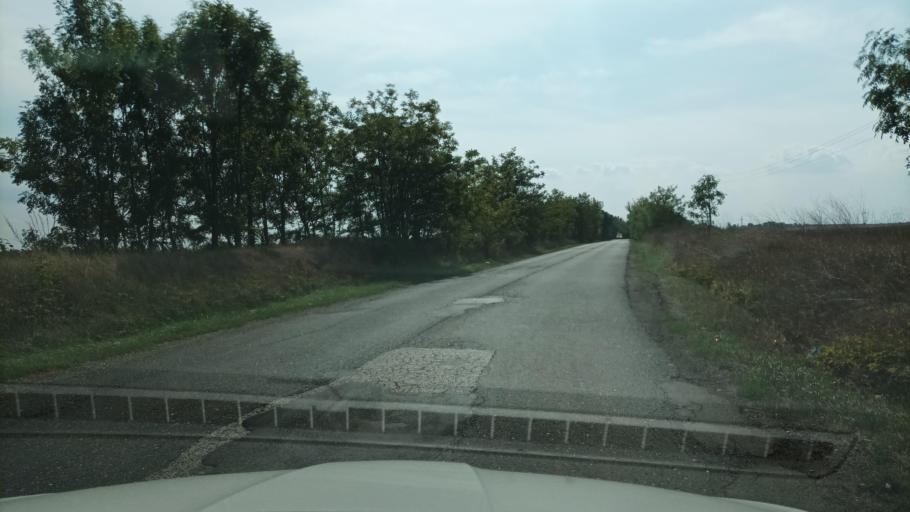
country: HU
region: Heves
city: Hatvan
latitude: 47.6460
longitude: 19.6445
